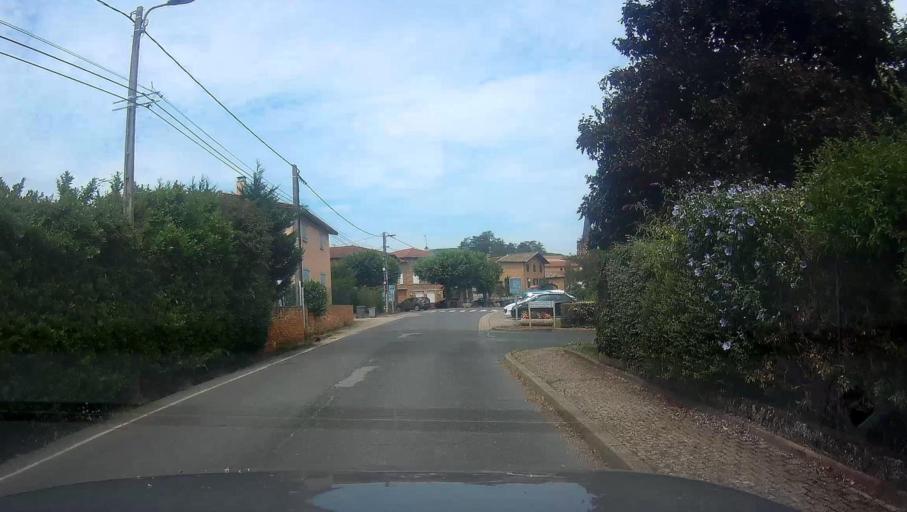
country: FR
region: Rhone-Alpes
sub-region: Departement du Rhone
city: Theize
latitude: 45.9237
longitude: 4.6186
